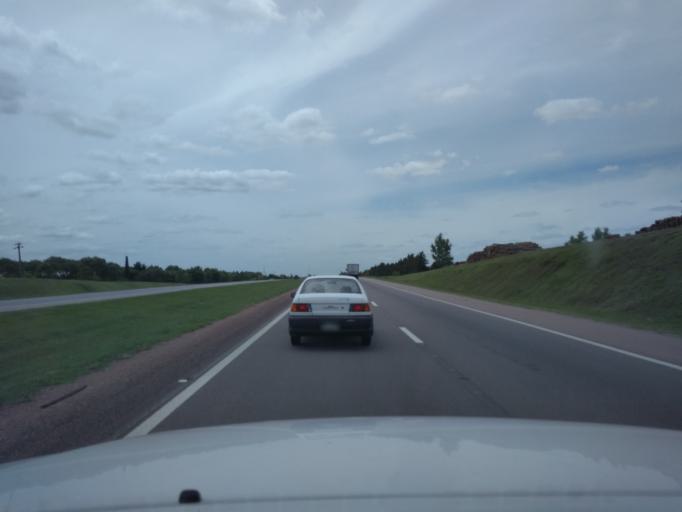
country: UY
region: Canelones
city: La Paz
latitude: -34.7426
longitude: -56.2518
